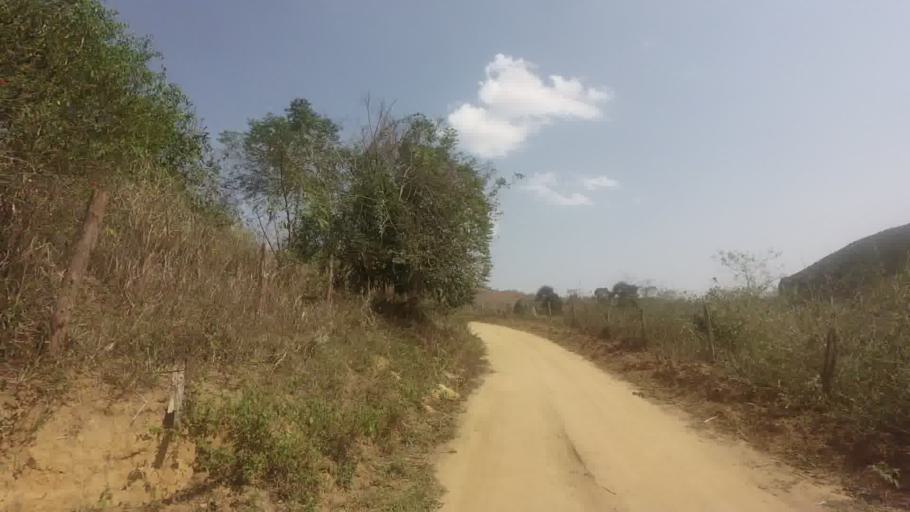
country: BR
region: Espirito Santo
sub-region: Sao Jose Do Calcado
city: Sao Jose do Calcado
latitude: -21.0235
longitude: -41.5186
